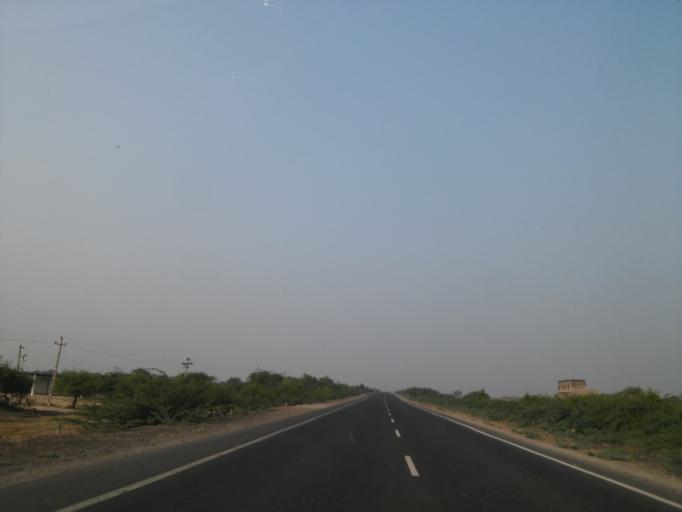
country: IN
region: Gujarat
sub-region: Kachchh
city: Anjar
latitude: 23.2959
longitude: 70.0583
